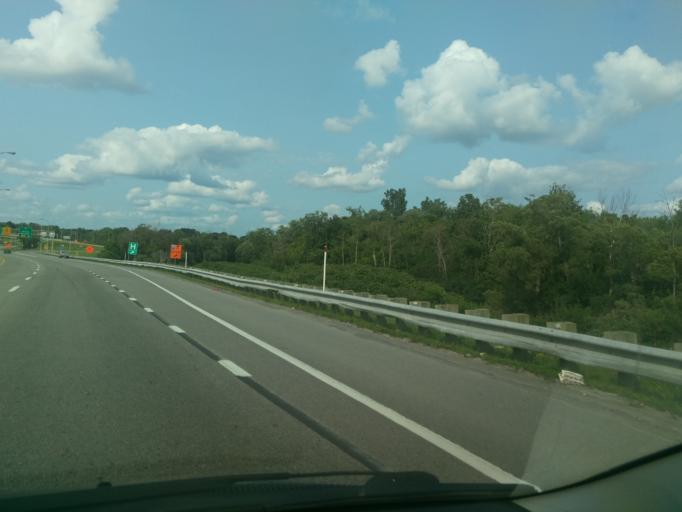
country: CA
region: Ontario
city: Ottawa
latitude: 45.4423
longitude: -75.7234
